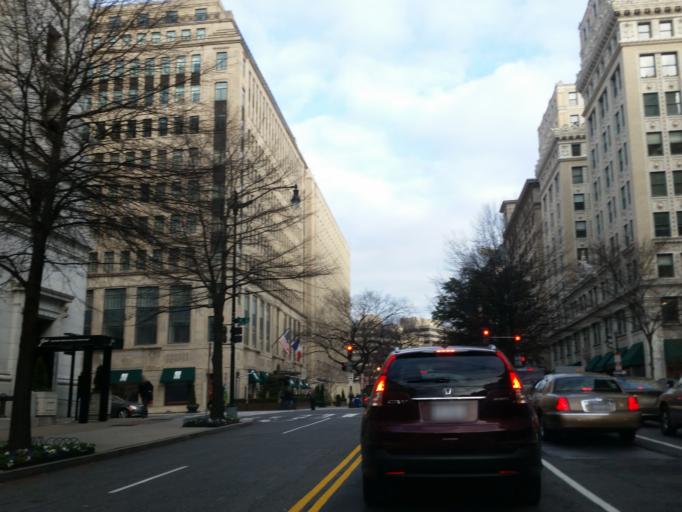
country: US
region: Washington, D.C.
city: Washington, D.C.
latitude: 38.8997
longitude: -77.0336
